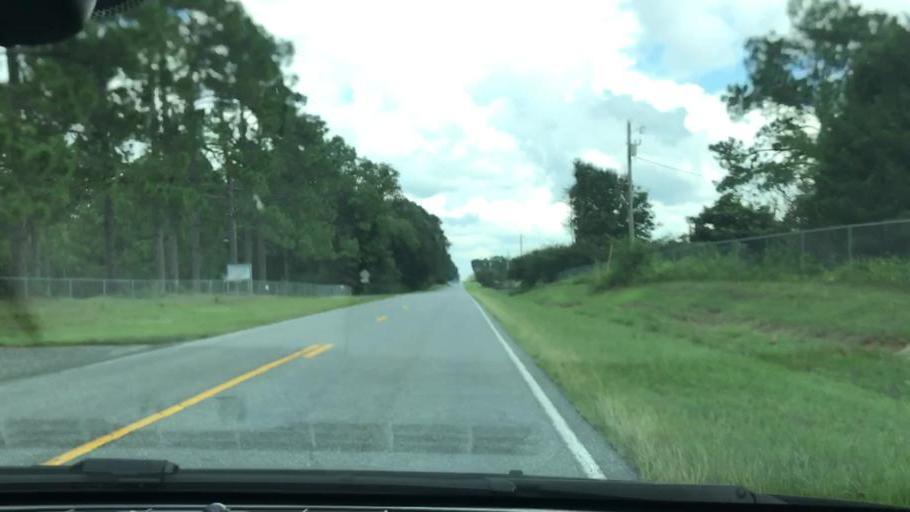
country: US
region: Florida
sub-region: Jackson County
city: Malone
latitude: 30.8915
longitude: -85.1474
